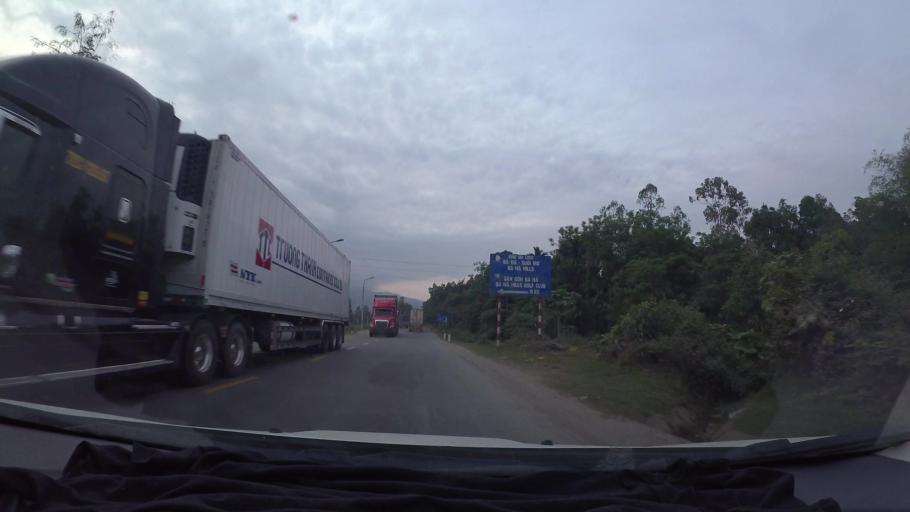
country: VN
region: Da Nang
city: Lien Chieu
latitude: 16.0552
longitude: 108.1017
